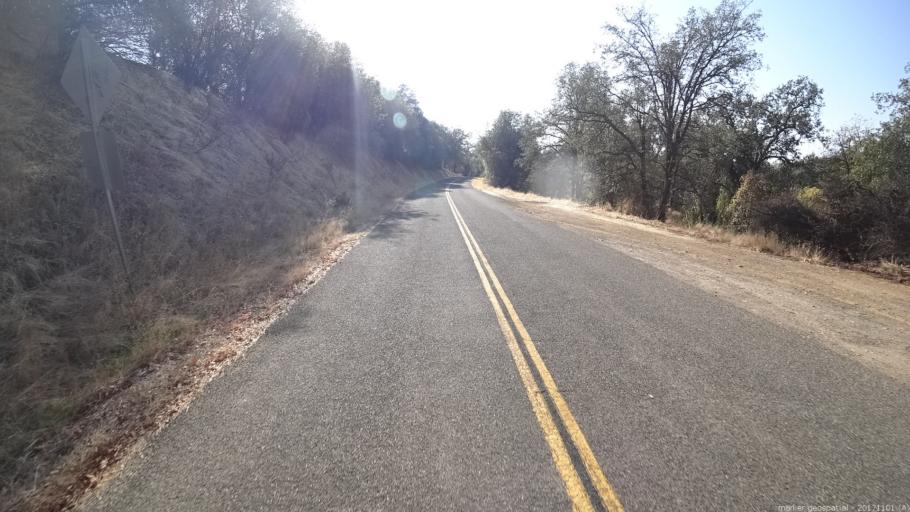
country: US
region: California
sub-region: Shasta County
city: Shasta Lake
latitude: 40.7154
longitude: -122.3288
